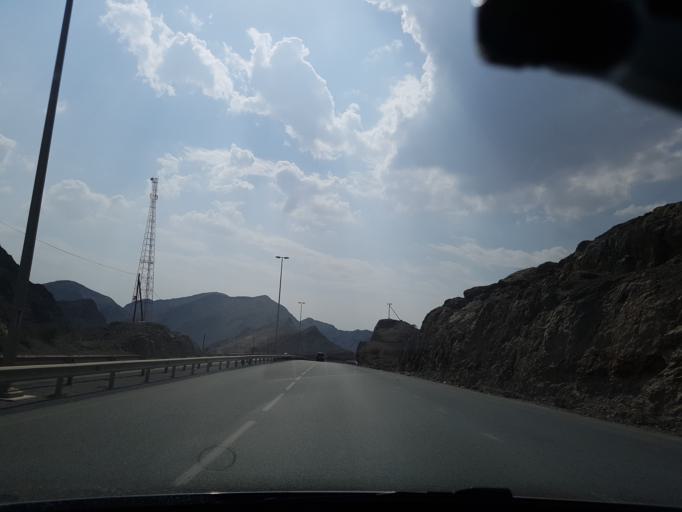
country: AE
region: Al Fujayrah
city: Dibba Al-Fujairah
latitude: 25.5225
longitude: 56.1045
